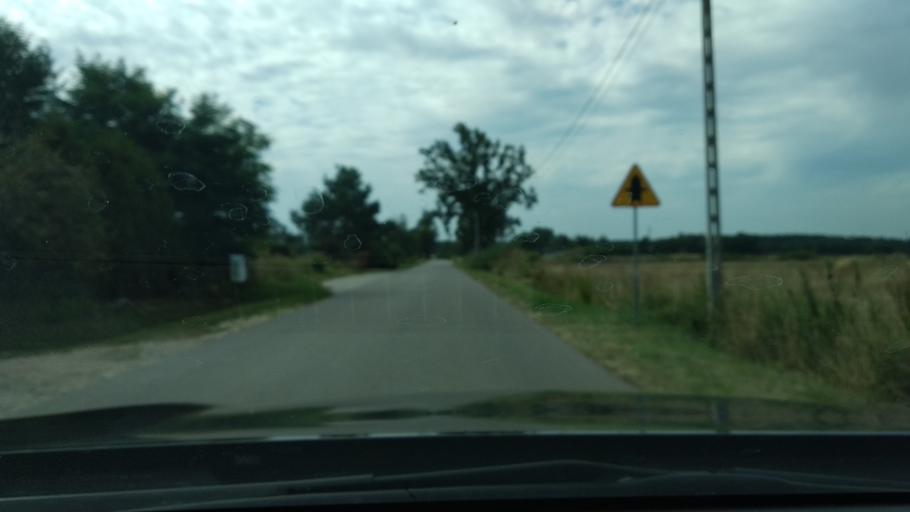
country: PL
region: Masovian Voivodeship
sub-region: Powiat pultuski
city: Zatory
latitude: 52.6522
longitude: 21.1862
